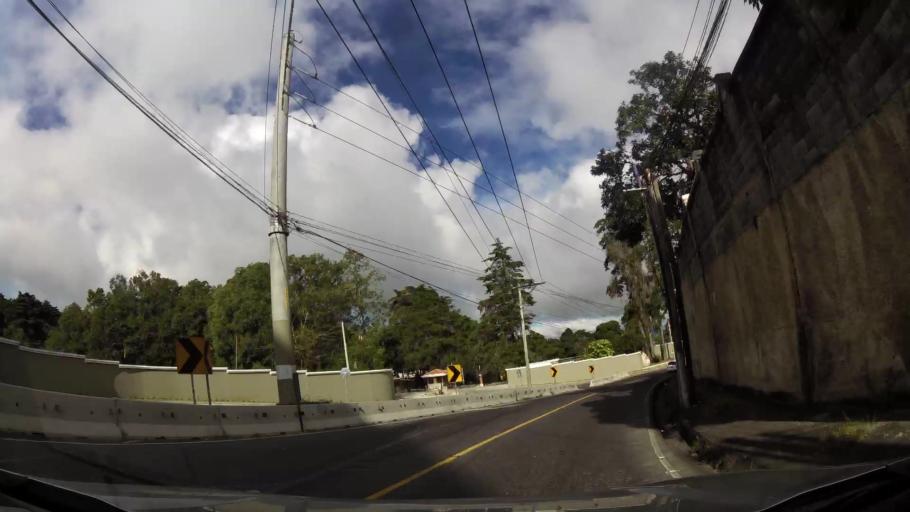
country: GT
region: Guatemala
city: Santa Catarina Pinula
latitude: 14.5617
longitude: -90.4790
